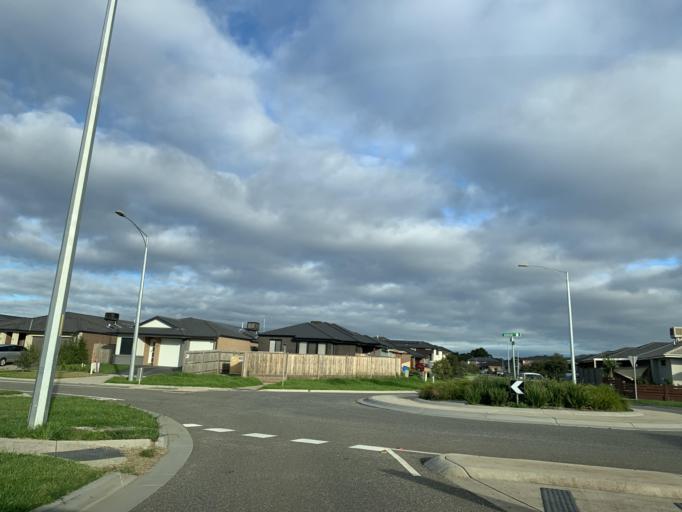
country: AU
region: Victoria
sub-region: Casey
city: Junction Village
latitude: -38.1267
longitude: 145.2984
